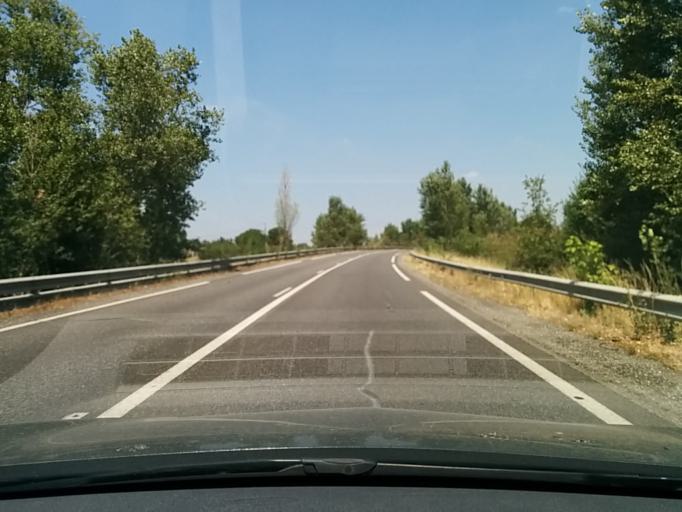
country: FR
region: Midi-Pyrenees
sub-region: Departement de la Haute-Garonne
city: Labege
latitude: 43.5253
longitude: 1.5226
